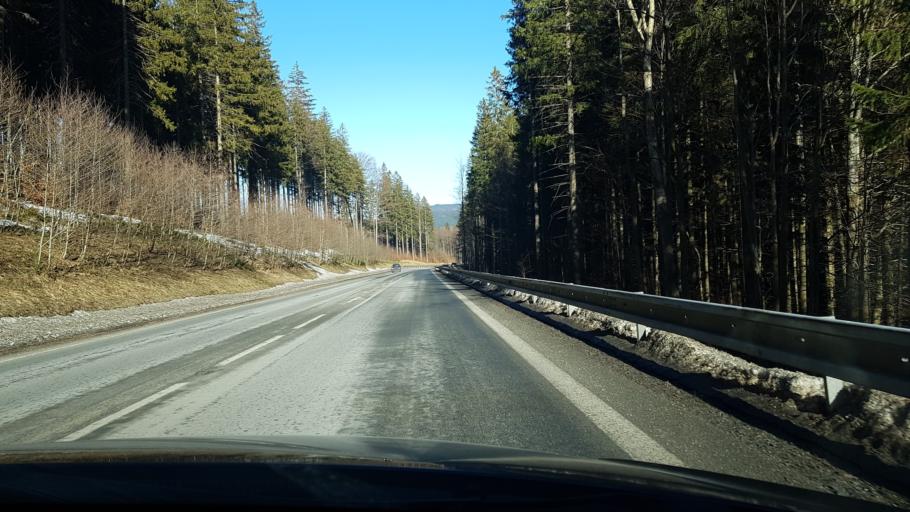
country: CZ
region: Olomoucky
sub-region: Okres Jesenik
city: Jesenik
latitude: 50.1504
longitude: 17.1672
